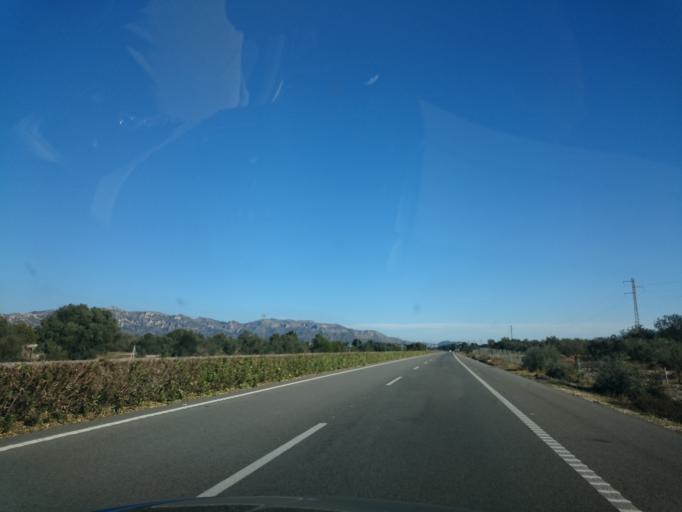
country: ES
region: Catalonia
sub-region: Provincia de Tarragona
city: l'Ametlla de Mar
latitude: 40.8948
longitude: 0.8074
